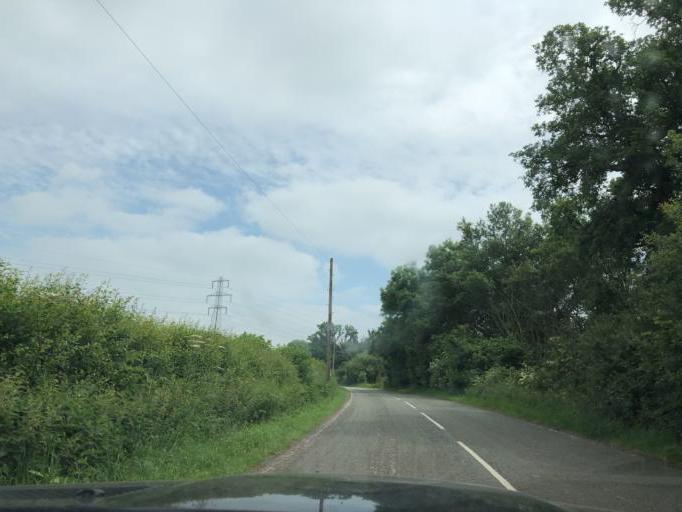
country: GB
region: England
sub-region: Warwickshire
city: Kenilworth
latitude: 52.3313
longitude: -1.6155
